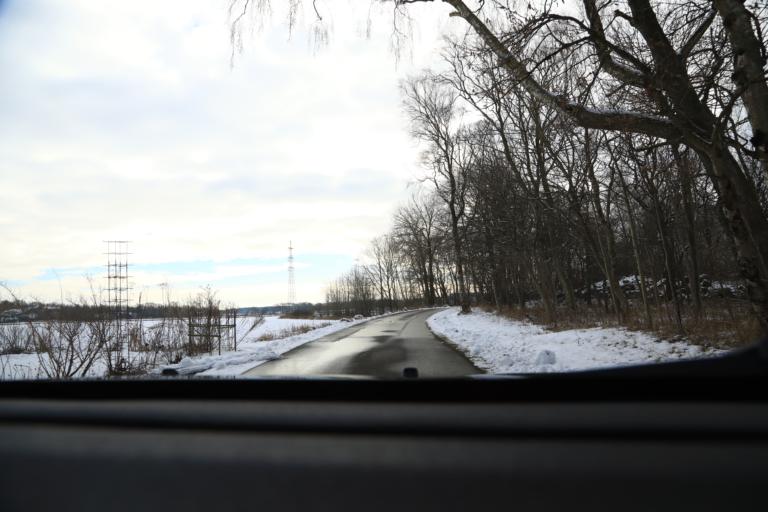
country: SE
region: Halland
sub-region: Kungsbacka Kommun
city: Frillesas
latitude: 57.2312
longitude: 12.1908
